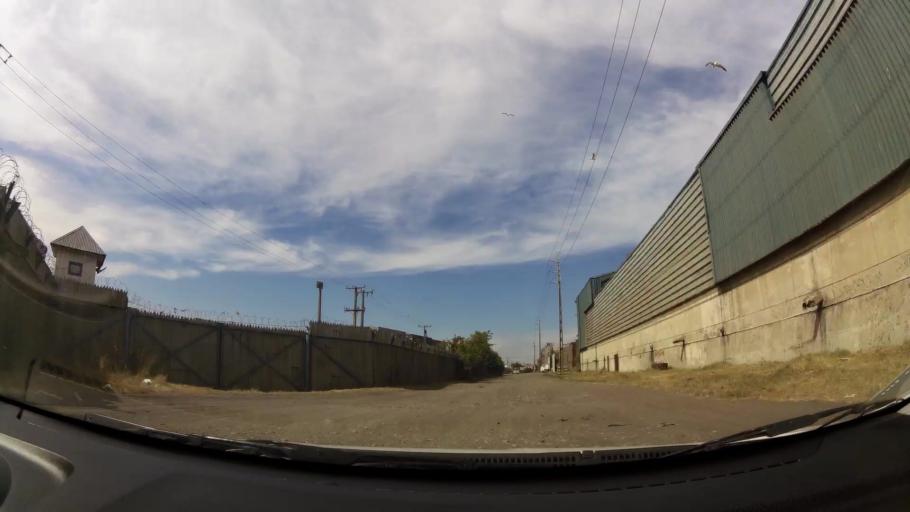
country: CL
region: Biobio
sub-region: Provincia de Concepcion
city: Talcahuano
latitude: -36.7275
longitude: -73.1159
